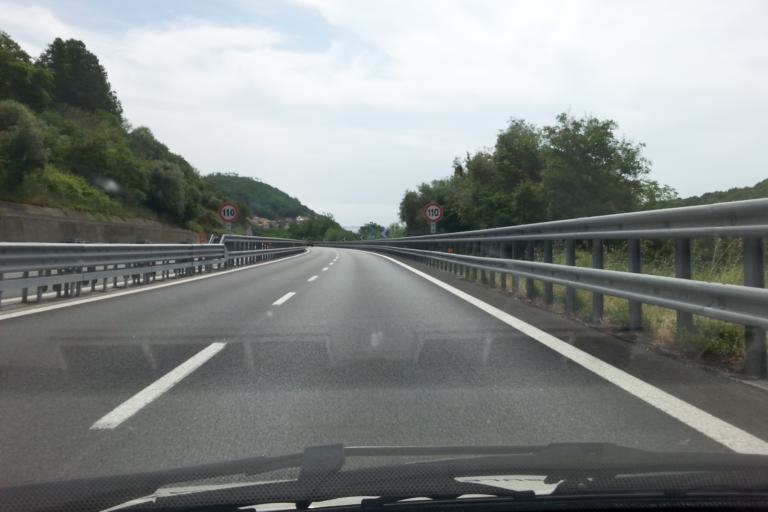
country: IT
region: Liguria
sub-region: Provincia di Savona
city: Vezzi Portio
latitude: 44.2267
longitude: 8.3755
